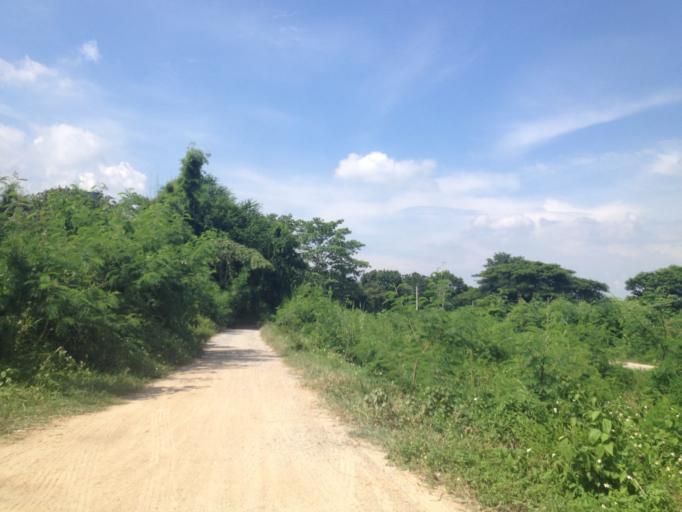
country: TH
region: Chiang Mai
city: Chiang Mai
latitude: 18.7520
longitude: 98.9424
